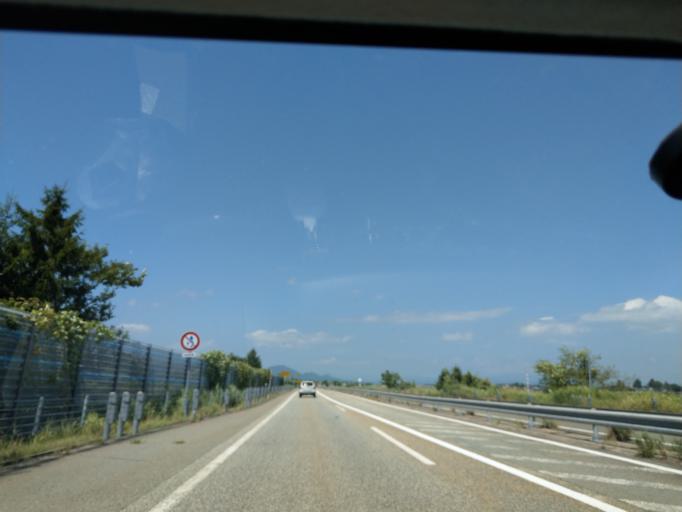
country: JP
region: Akita
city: Omagari
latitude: 39.3710
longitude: 140.4848
